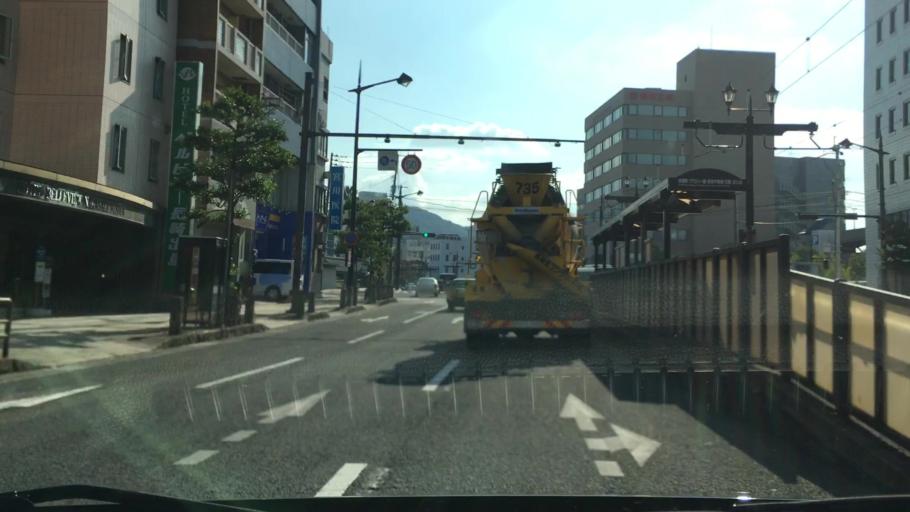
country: JP
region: Nagasaki
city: Nagasaki-shi
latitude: 32.7456
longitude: 129.8721
